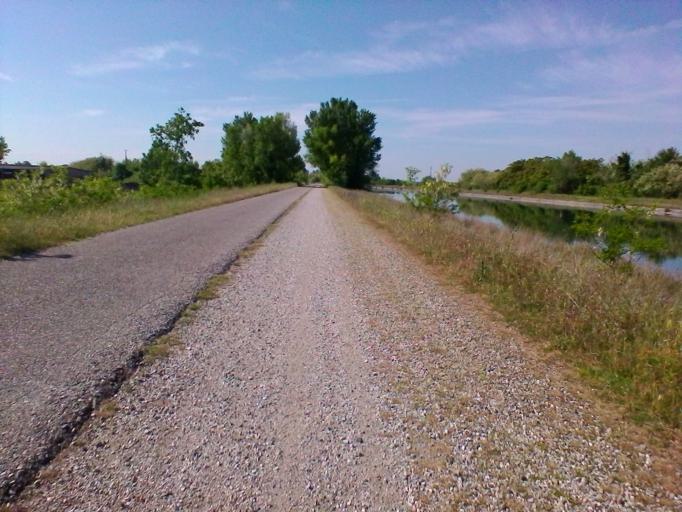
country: IT
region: Lombardy
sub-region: Provincia di Mantova
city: Roverbella
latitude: 45.2745
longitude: 10.7297
